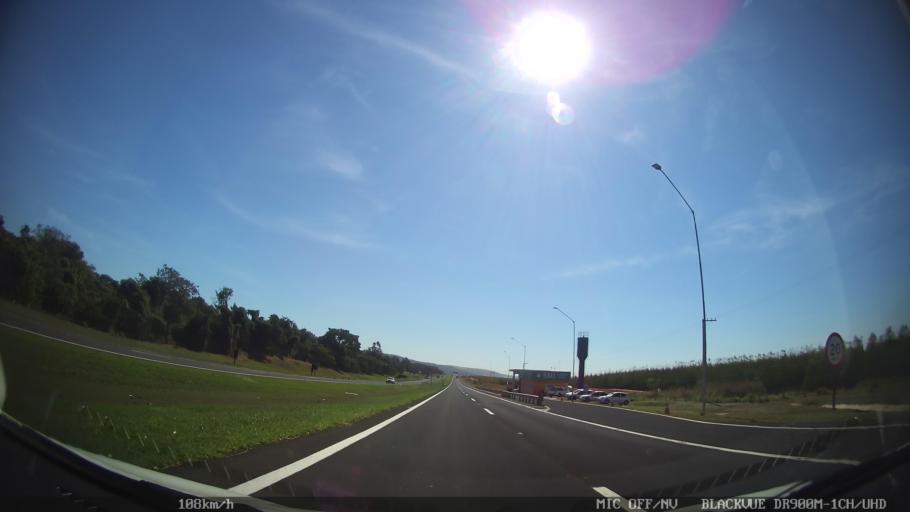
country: BR
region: Sao Paulo
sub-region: Sao Simao
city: Sao Simao
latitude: -21.5448
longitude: -47.6392
